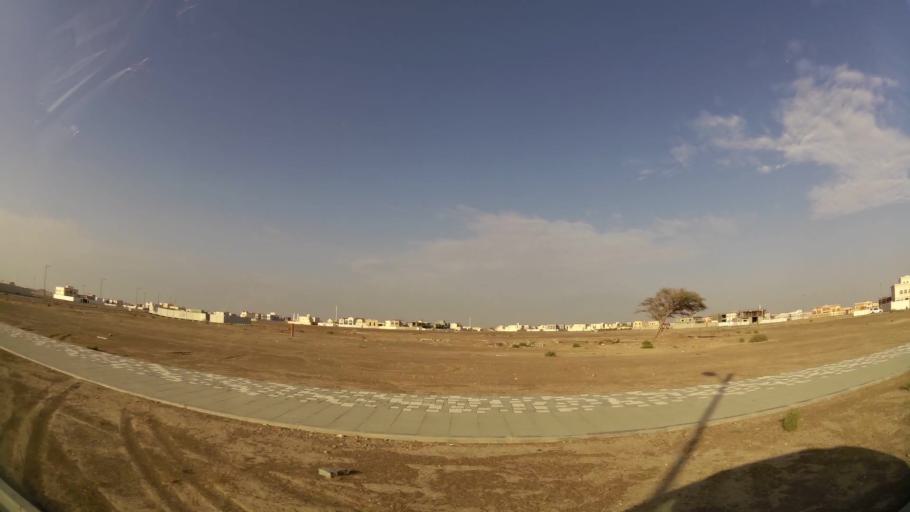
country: AE
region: Abu Dhabi
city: Al Ain
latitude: 24.0987
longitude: 55.8474
